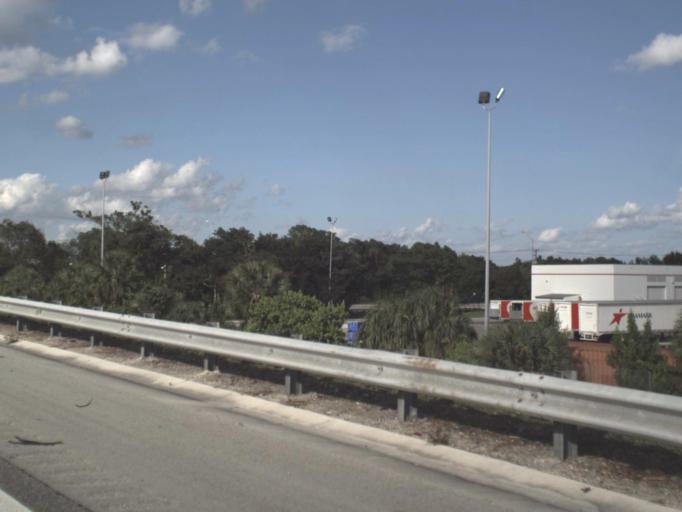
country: US
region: Florida
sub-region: Broward County
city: Coconut Creek
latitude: 26.2584
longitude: -80.1668
